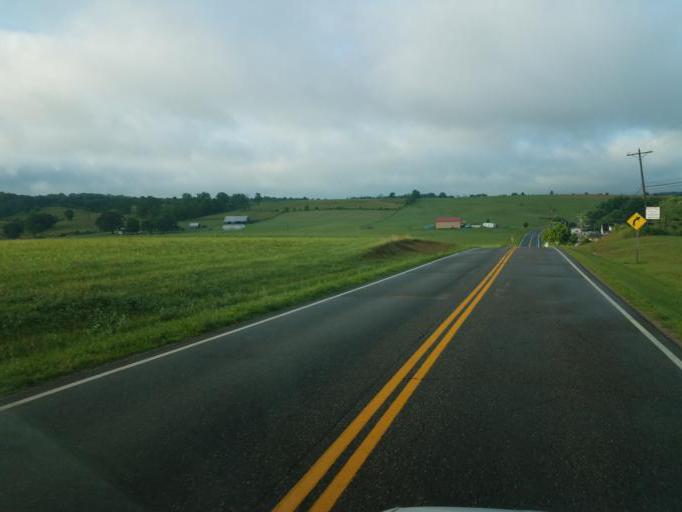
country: US
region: Ohio
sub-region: Jackson County
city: Oak Hill
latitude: 38.8294
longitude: -82.3952
